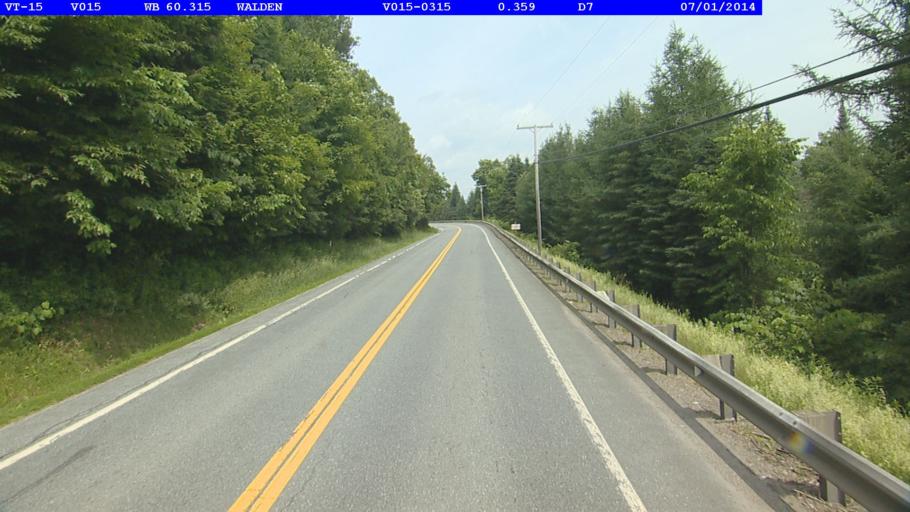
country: US
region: Vermont
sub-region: Caledonia County
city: Hardwick
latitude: 44.4800
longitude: -72.3018
